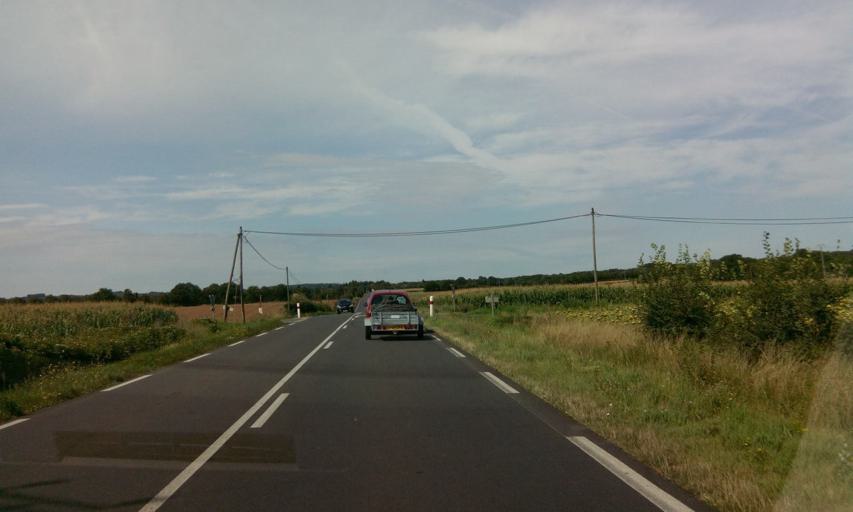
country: FR
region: Poitou-Charentes
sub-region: Departement de la Vienne
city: Chaunay
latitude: 46.1403
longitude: 0.1978
